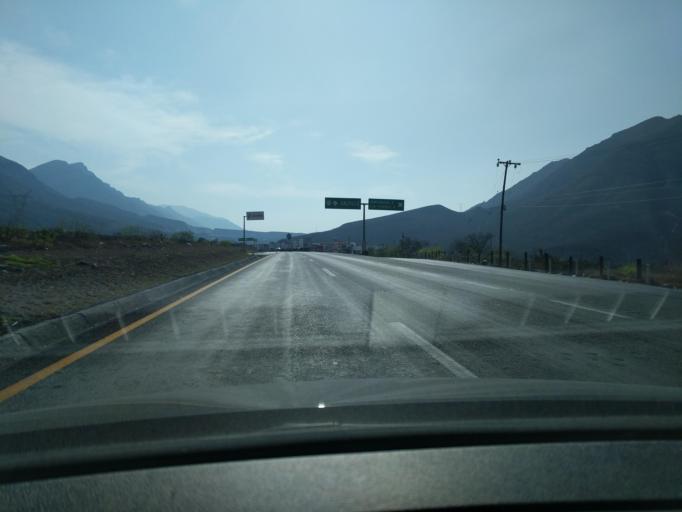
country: MX
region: Nuevo Leon
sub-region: Garcia
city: Las Torres de Guadalupe
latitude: 25.6613
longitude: -100.7123
